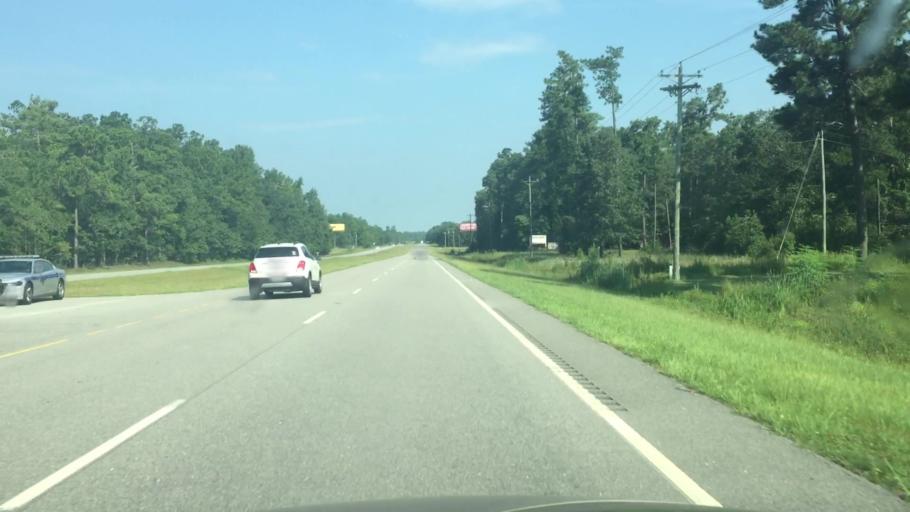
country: US
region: South Carolina
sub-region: Horry County
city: Loris
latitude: 34.0563
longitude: -78.8432
